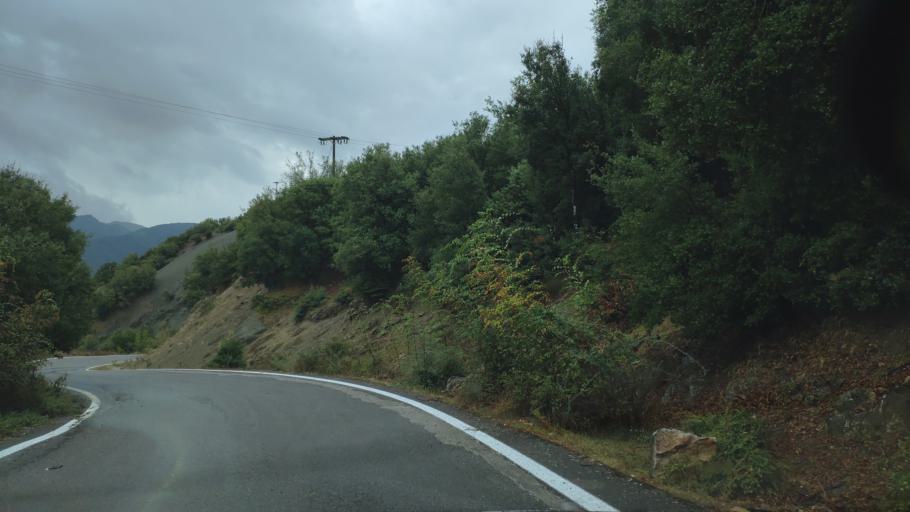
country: GR
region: Thessaly
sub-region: Nomos Kardhitsas
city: Anthiro
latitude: 39.1084
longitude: 21.4125
